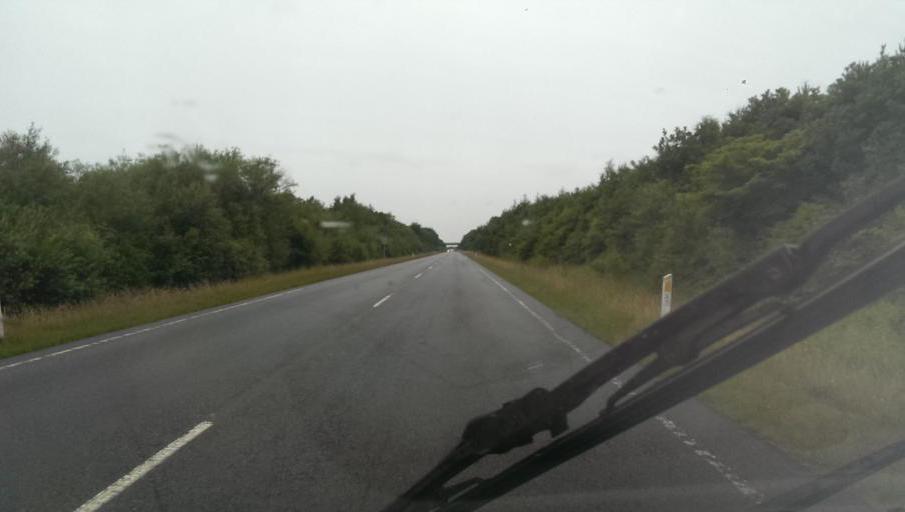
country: DK
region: South Denmark
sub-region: Esbjerg Kommune
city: Esbjerg
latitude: 55.5266
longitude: 8.4411
